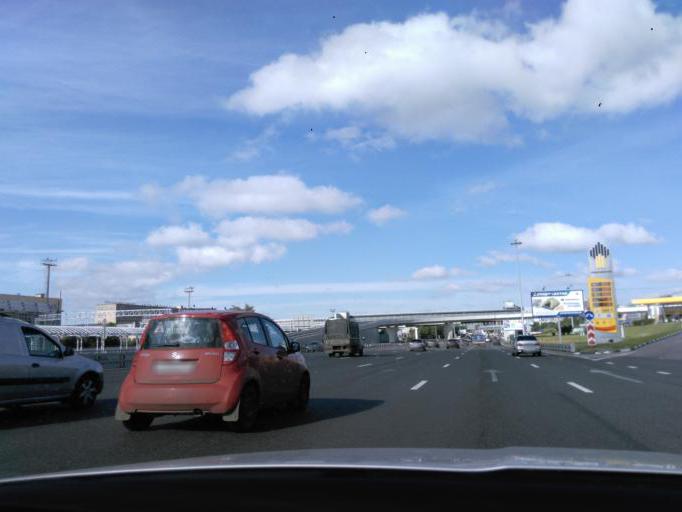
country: RU
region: Moscow
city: Taganskiy
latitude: 55.7196
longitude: 37.6986
